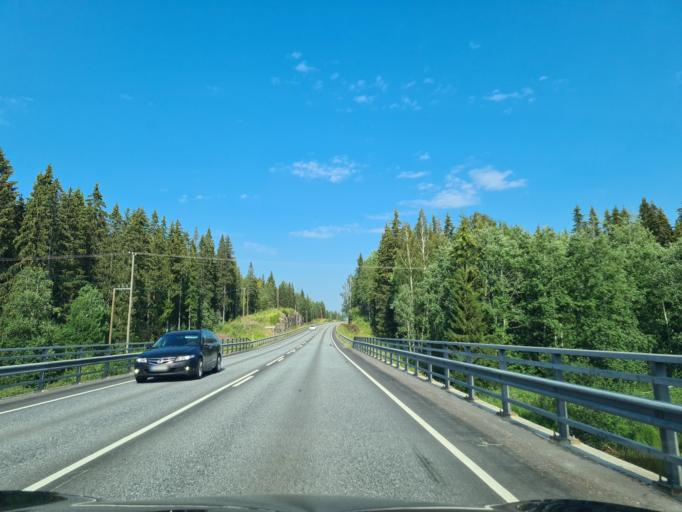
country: FI
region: Satakunta
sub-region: Pori
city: Laengelmaeki
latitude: 61.7861
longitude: 22.2247
